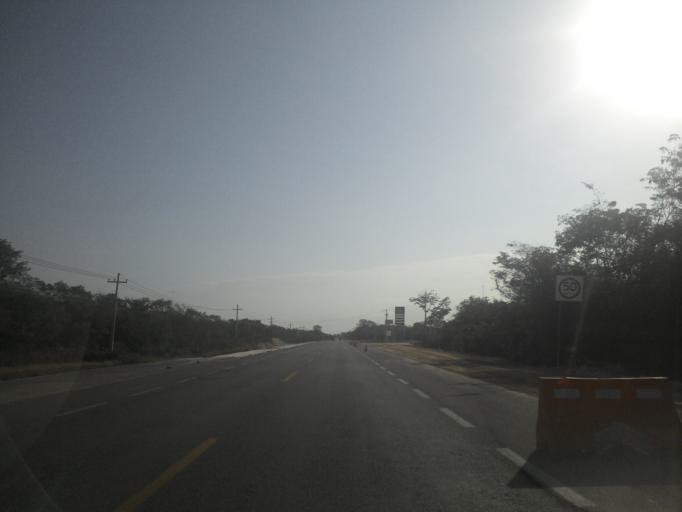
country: MX
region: Yucatan
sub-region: Valladolid
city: Tikuch
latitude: 20.6989
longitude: -88.1373
